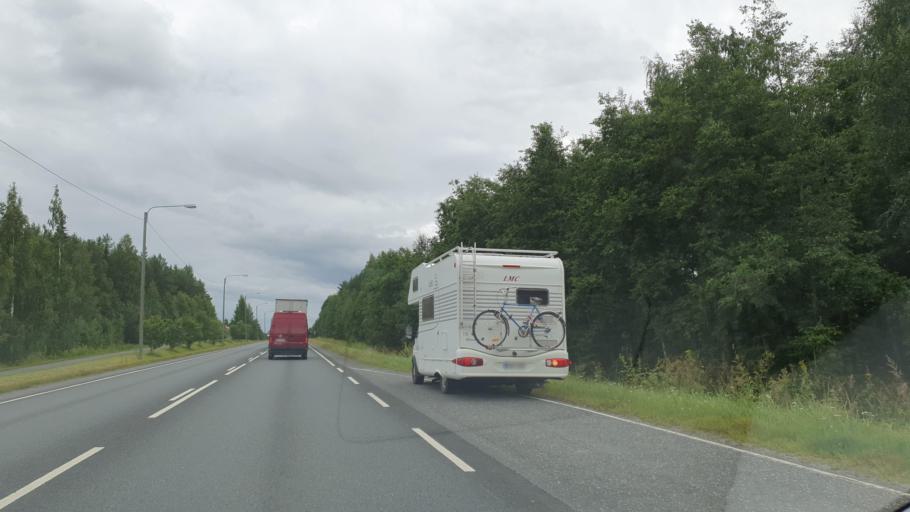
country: FI
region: Northern Savo
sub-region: Ylae-Savo
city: Lapinlahti
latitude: 63.4495
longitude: 27.3197
